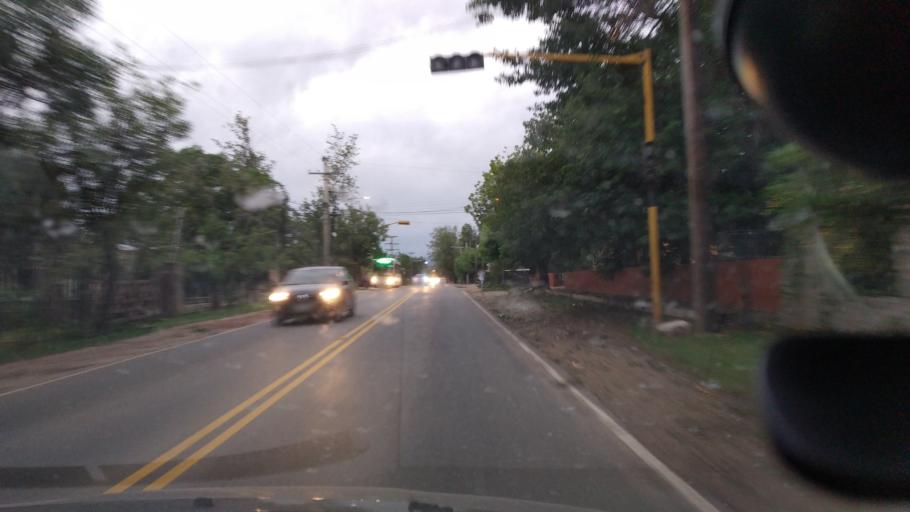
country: AR
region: Cordoba
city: Villa Las Rosas
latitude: -31.9182
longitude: -65.0384
